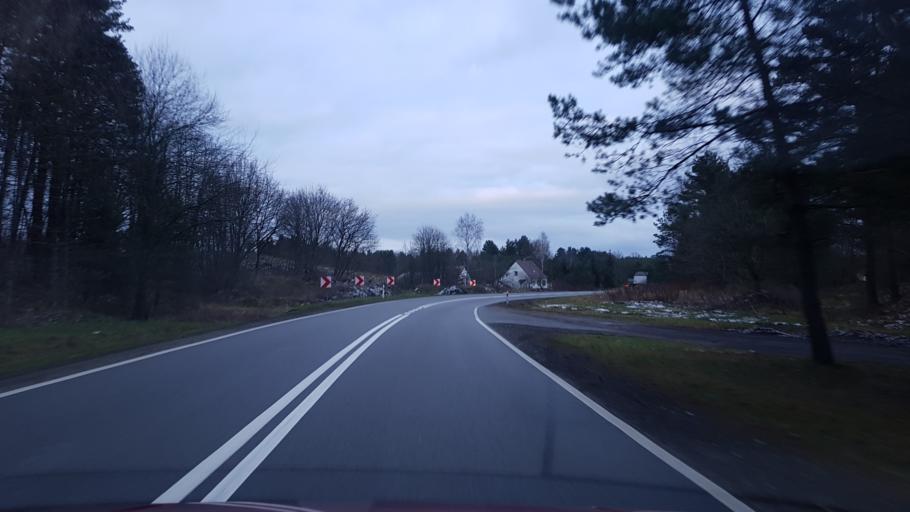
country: PL
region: Pomeranian Voivodeship
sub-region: Powiat bytowski
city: Tuchomie
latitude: 54.0382
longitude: 17.1954
